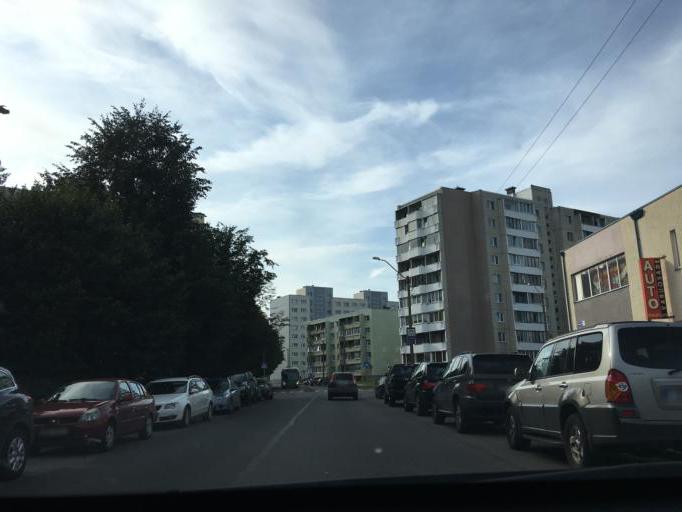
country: EE
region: Harju
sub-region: Tallinna linn
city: Kose
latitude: 59.4499
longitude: 24.8741
